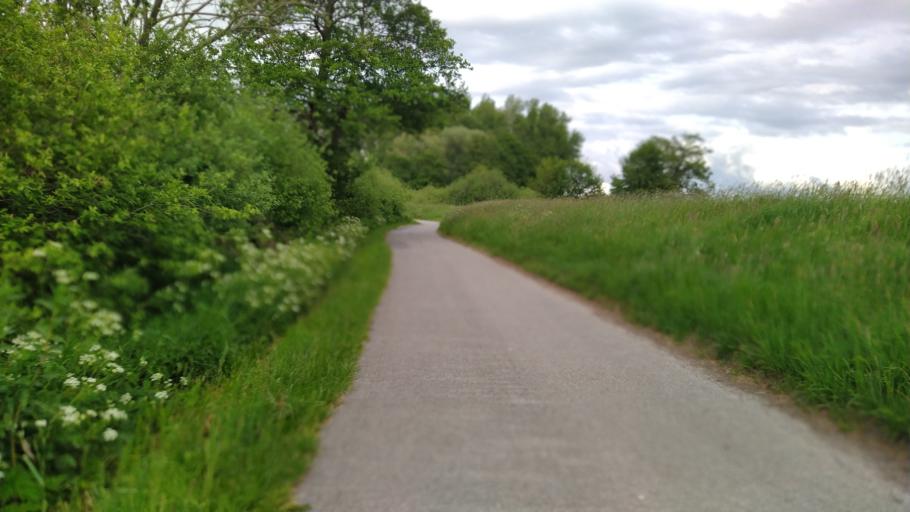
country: DE
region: Lower Saxony
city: Buxtehude
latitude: 53.4918
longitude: 9.7246
